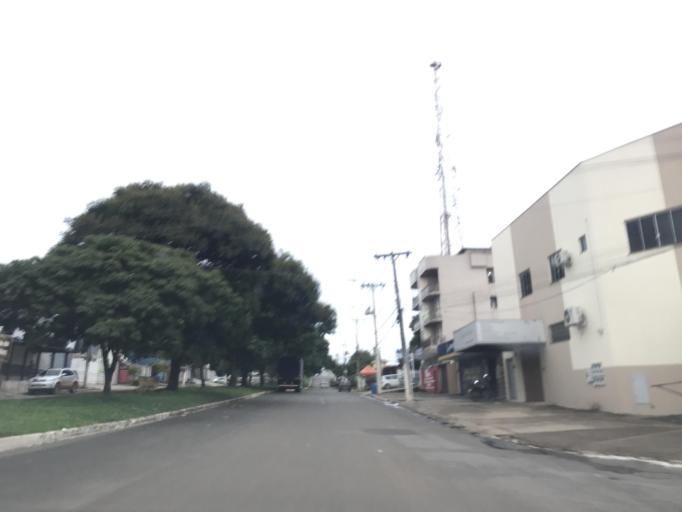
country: BR
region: Goias
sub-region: Luziania
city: Luziania
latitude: -16.2578
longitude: -47.9589
